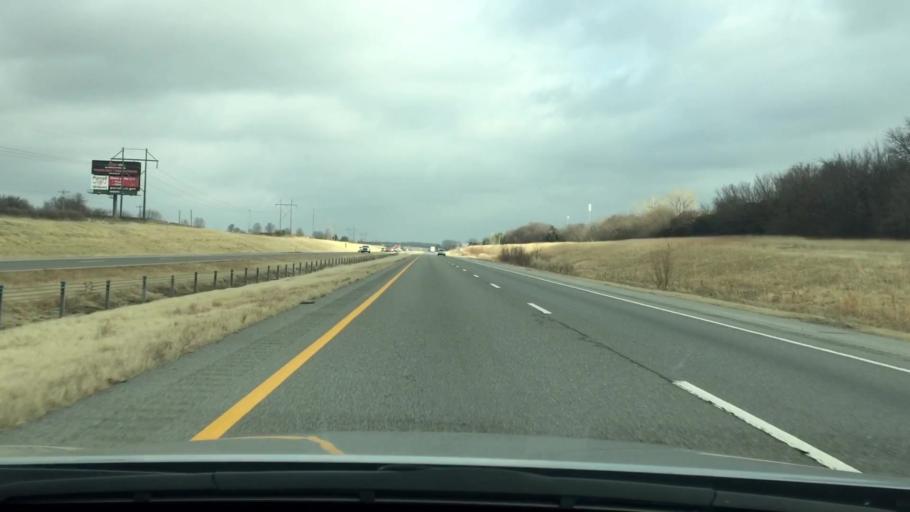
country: US
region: Oklahoma
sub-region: McClain County
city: Purcell
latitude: 35.0191
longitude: -97.3758
